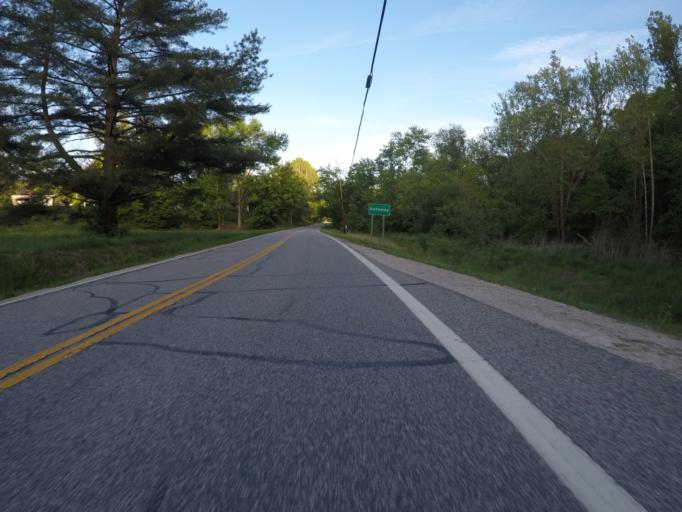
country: US
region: West Virginia
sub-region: Cabell County
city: Huntington
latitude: 38.4899
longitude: -82.4764
